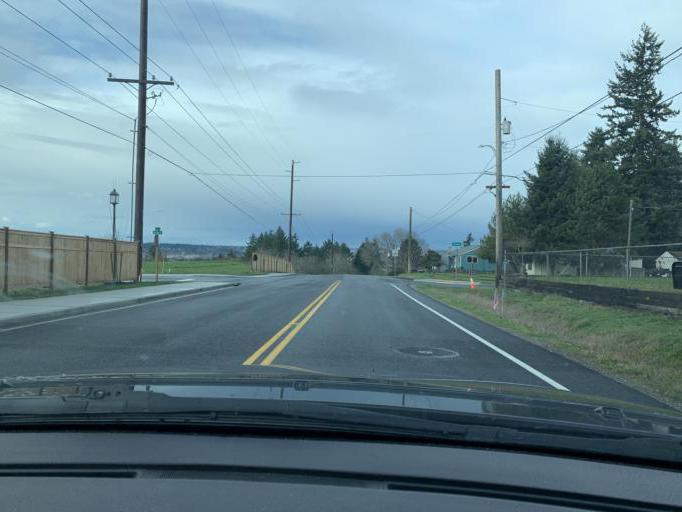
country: US
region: Washington
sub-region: Pierce County
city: Milton
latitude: 47.2391
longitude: -122.3183
